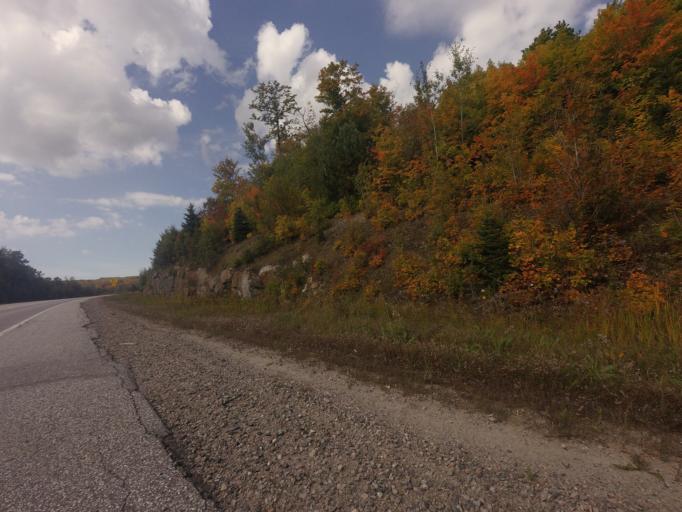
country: CA
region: Quebec
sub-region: Laurentides
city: Mont-Laurier
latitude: 46.5589
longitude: -75.6611
